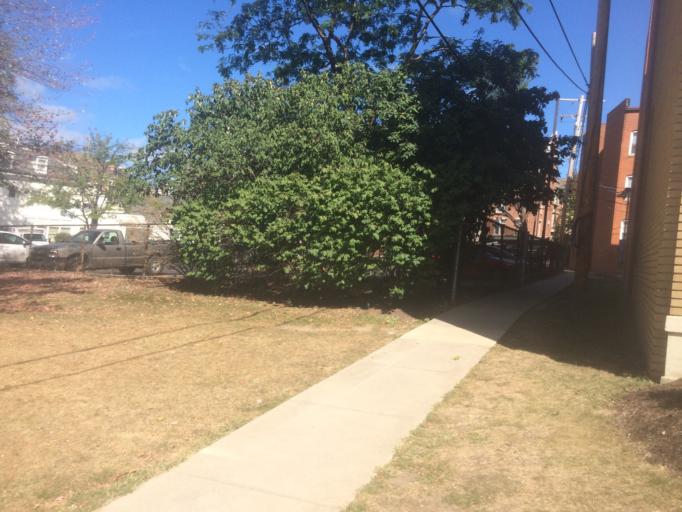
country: US
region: Ohio
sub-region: Cuyahoga County
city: East Cleveland
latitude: 41.5114
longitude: -81.6043
